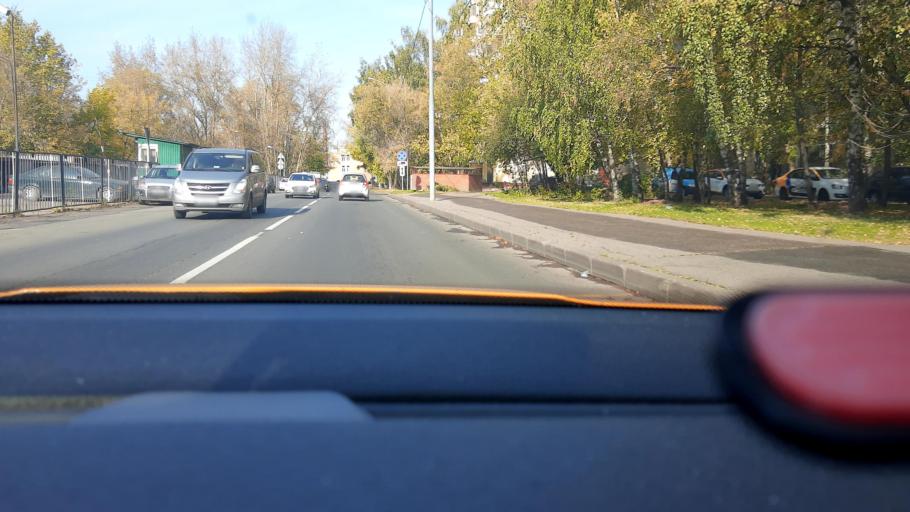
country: RU
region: Moscow
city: Vagonoremont
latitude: 55.8958
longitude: 37.5296
